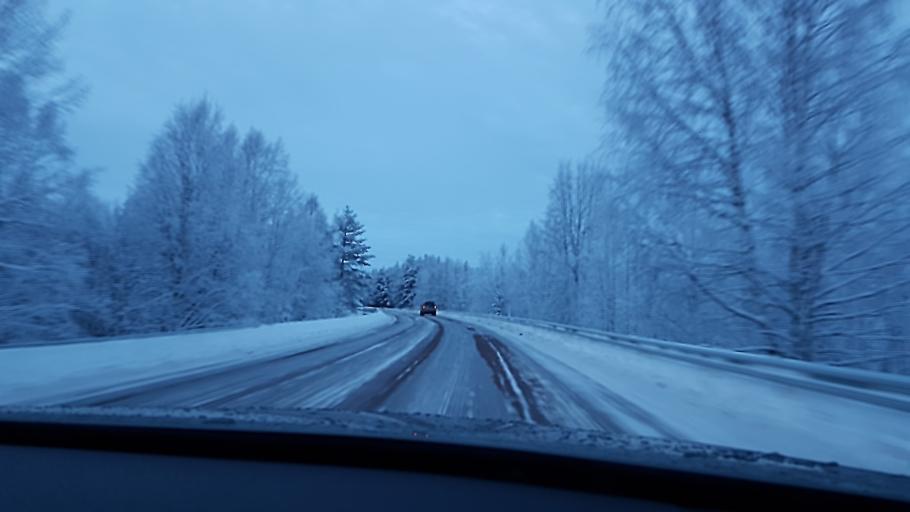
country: SE
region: Jaemtland
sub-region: Harjedalens Kommun
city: Sveg
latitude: 62.0517
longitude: 14.6403
